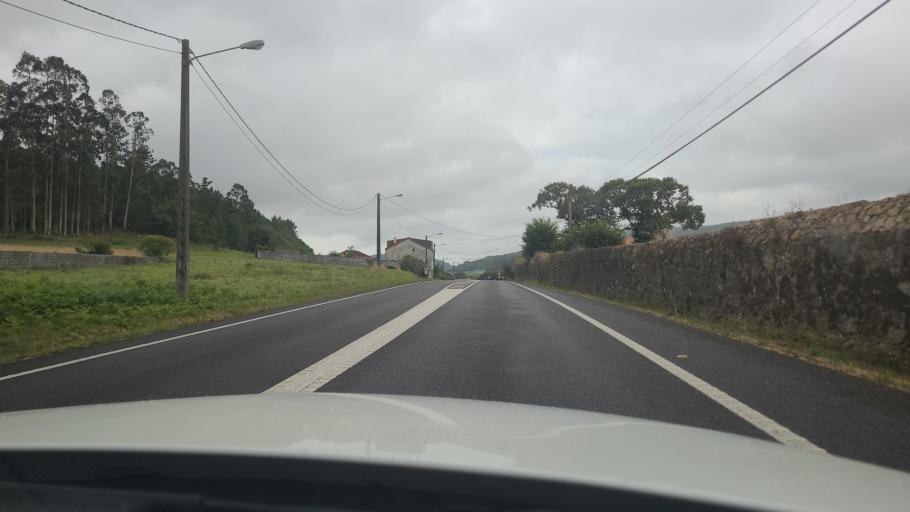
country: ES
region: Galicia
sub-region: Provincia da Coruna
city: Cee
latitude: 42.9953
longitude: -9.1806
